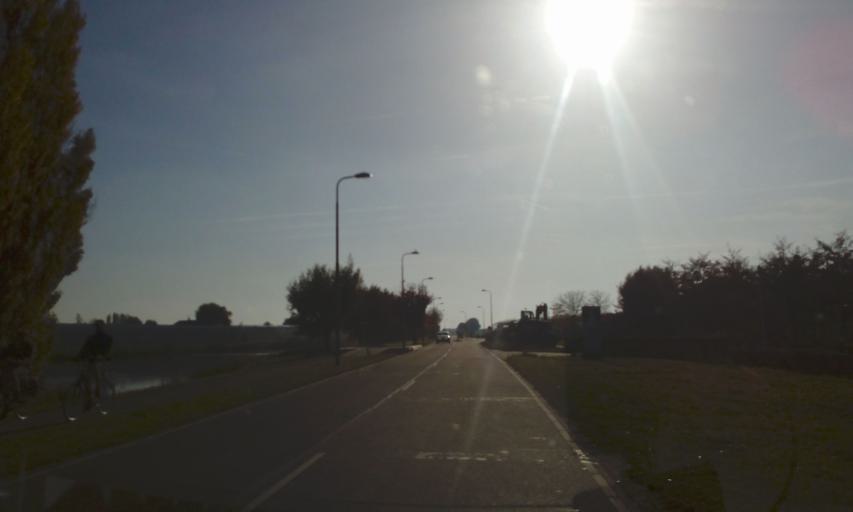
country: NL
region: South Holland
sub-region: Gemeente Zoetermeer
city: Zoetermeer
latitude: 52.0293
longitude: 4.5035
